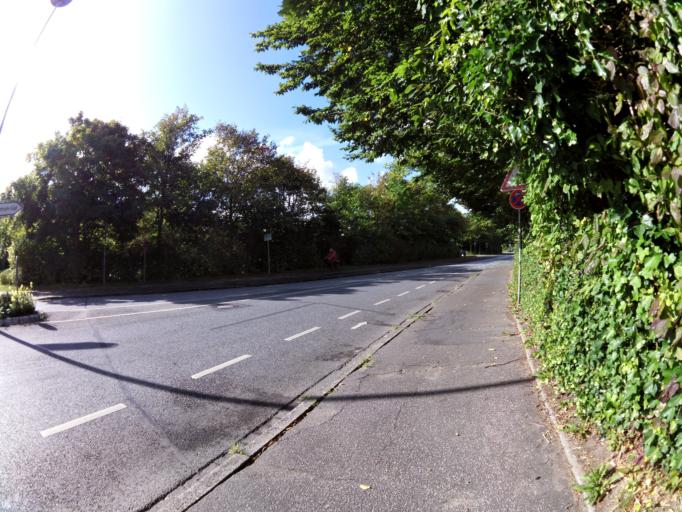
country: DE
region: Schleswig-Holstein
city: Eckernforde
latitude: 54.4492
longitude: 9.8442
